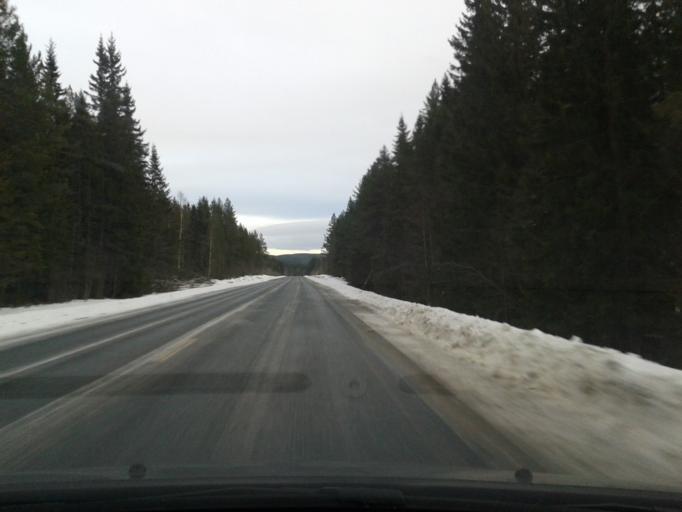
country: SE
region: Vaesternorrland
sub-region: Solleftea Kommun
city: As
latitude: 63.4413
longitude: 16.9206
